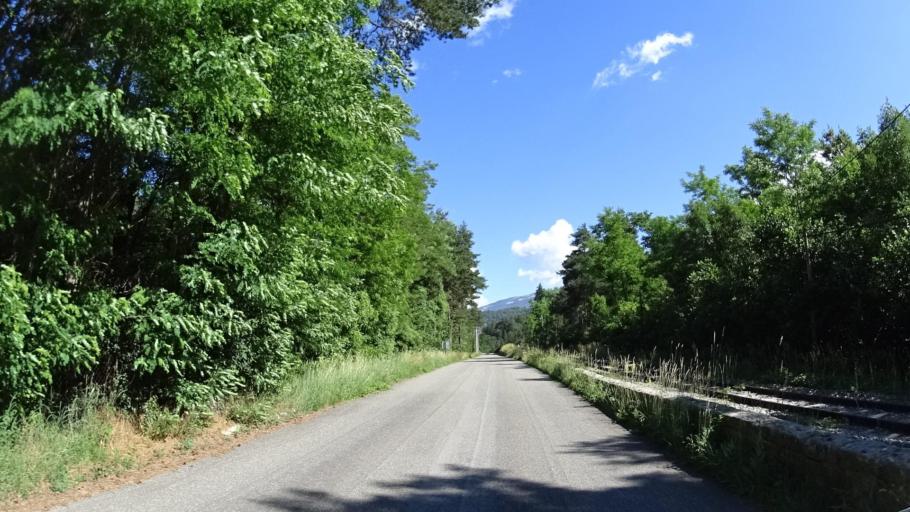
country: FR
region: Provence-Alpes-Cote d'Azur
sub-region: Departement des Alpes-de-Haute-Provence
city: Annot
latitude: 43.9864
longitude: 6.6480
